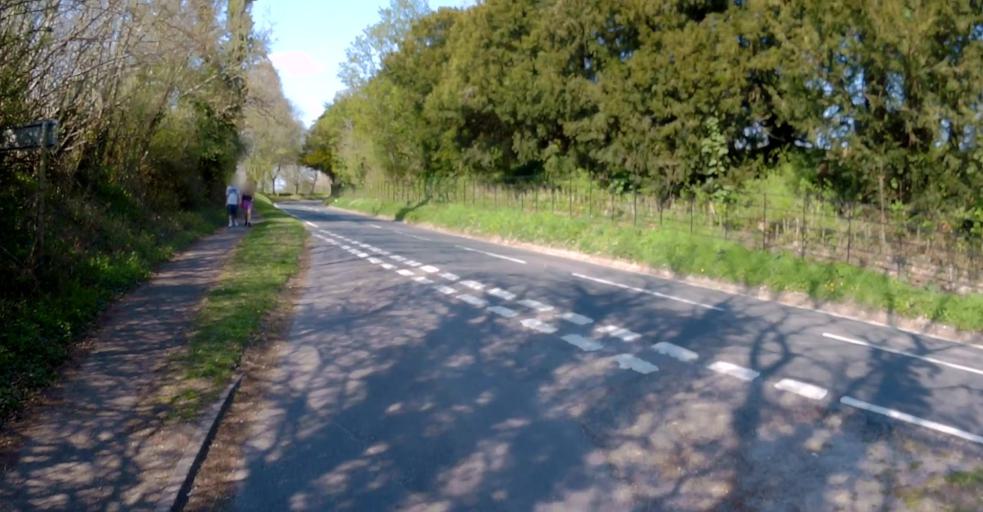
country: GB
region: England
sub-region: Hampshire
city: Four Marks
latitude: 51.0973
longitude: -1.1622
